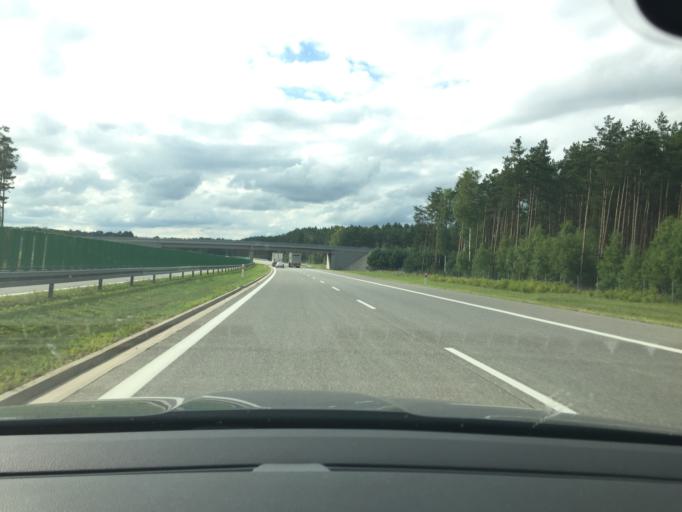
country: PL
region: Lubusz
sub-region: Powiat swiebodzinski
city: Lagow
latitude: 52.3030
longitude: 15.2560
